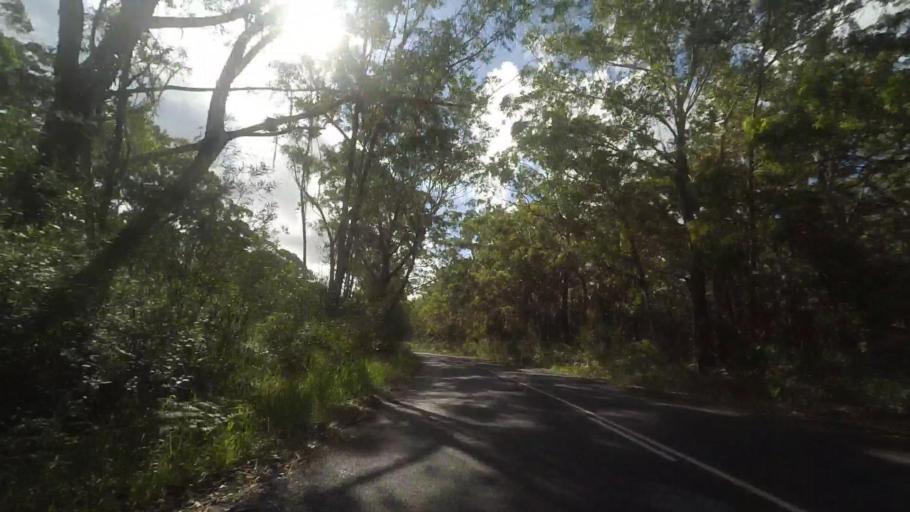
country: AU
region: New South Wales
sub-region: Great Lakes
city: Forster
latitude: -32.4215
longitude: 152.4927
